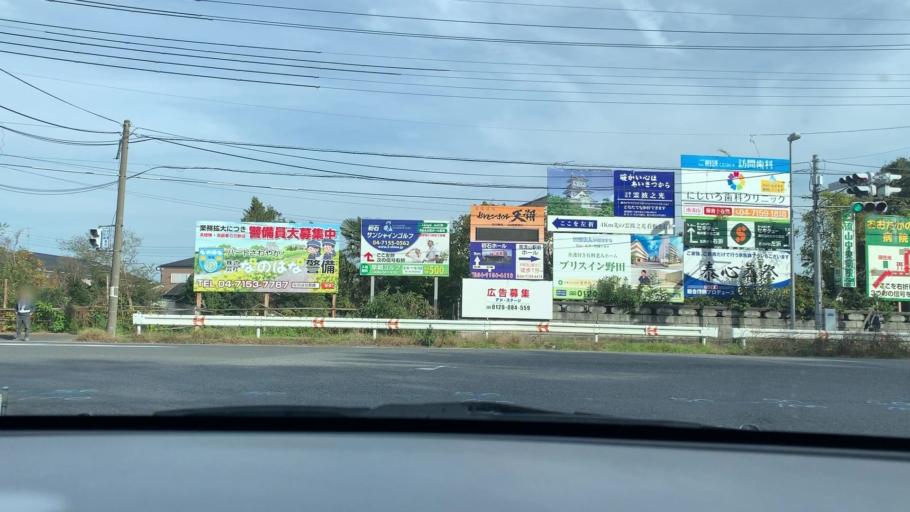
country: JP
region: Chiba
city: Nagareyama
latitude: 35.8822
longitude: 139.9023
